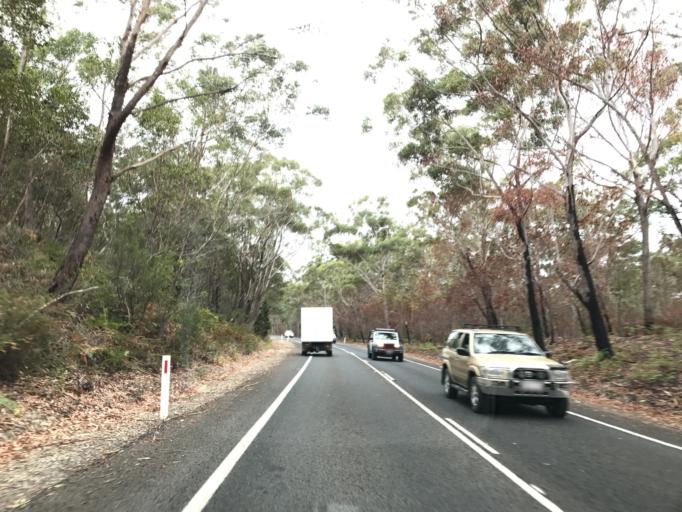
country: AU
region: Queensland
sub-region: Redland
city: Victoria Point
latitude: -27.4349
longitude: 153.5027
